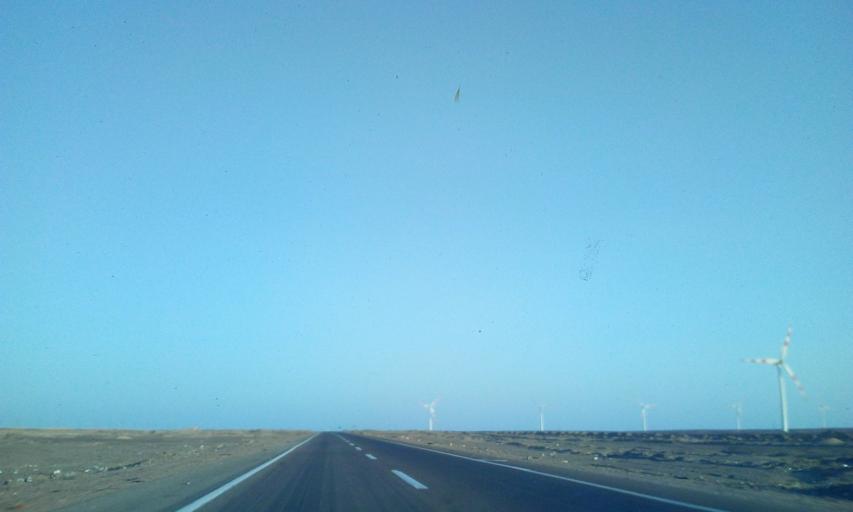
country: EG
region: South Sinai
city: Tor
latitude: 28.0742
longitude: 33.2586
